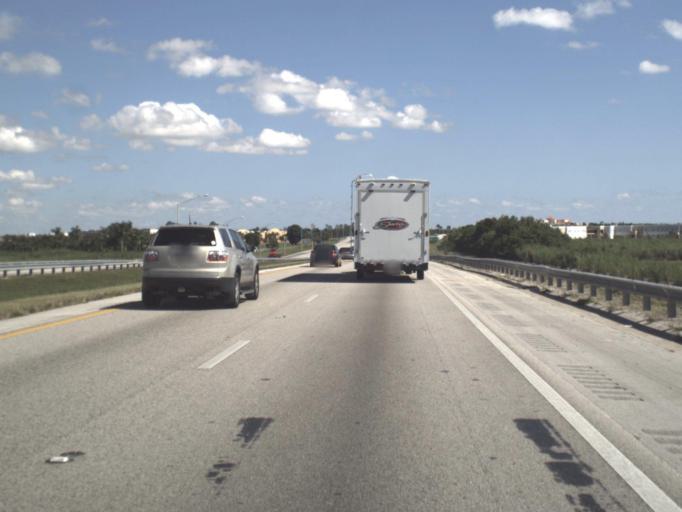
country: US
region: Florida
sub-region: Miami-Dade County
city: Homestead
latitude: 25.4695
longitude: -80.4519
